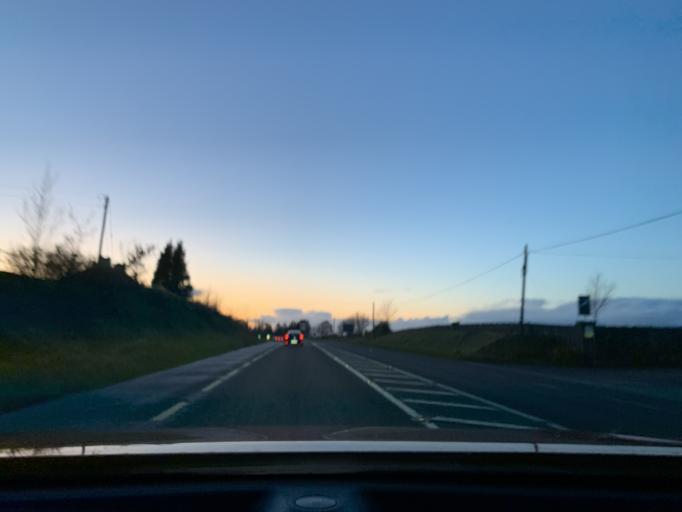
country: IE
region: Connaught
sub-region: Roscommon
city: Boyle
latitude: 53.9700
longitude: -8.2485
